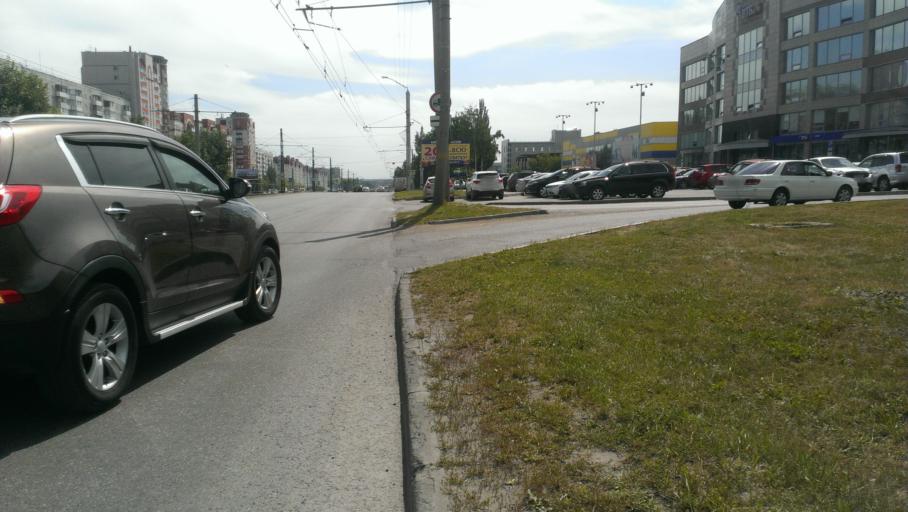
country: RU
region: Altai Krai
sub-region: Gorod Barnaulskiy
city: Barnaul
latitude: 53.3557
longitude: 83.6982
